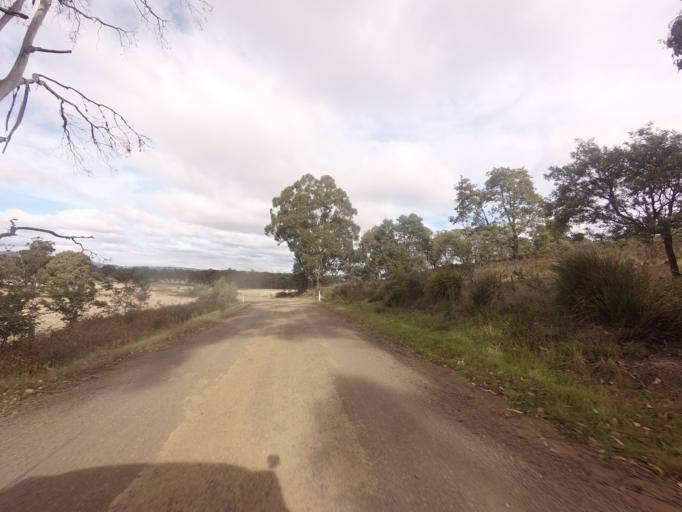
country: AU
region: Tasmania
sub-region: Brighton
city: Bridgewater
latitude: -42.4179
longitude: 147.4175
